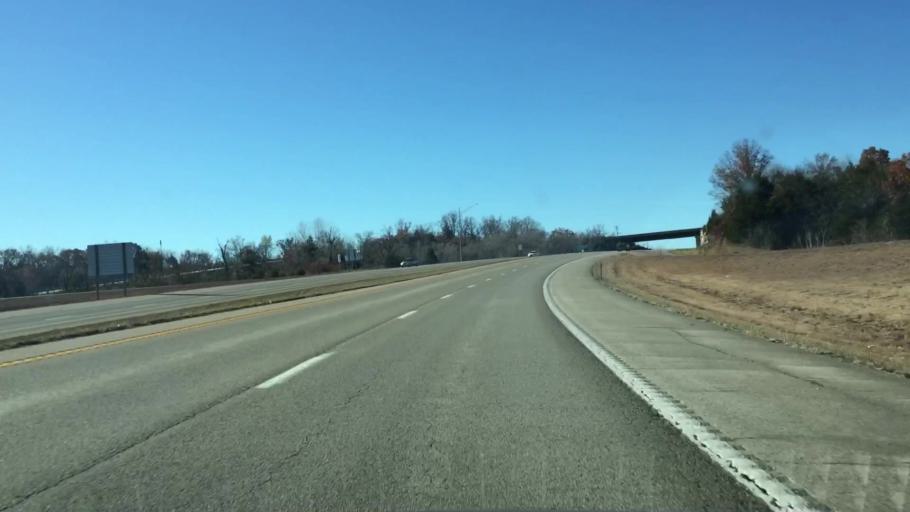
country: US
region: Missouri
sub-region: Cole County
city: Jefferson City
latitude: 38.5383
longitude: -92.2104
